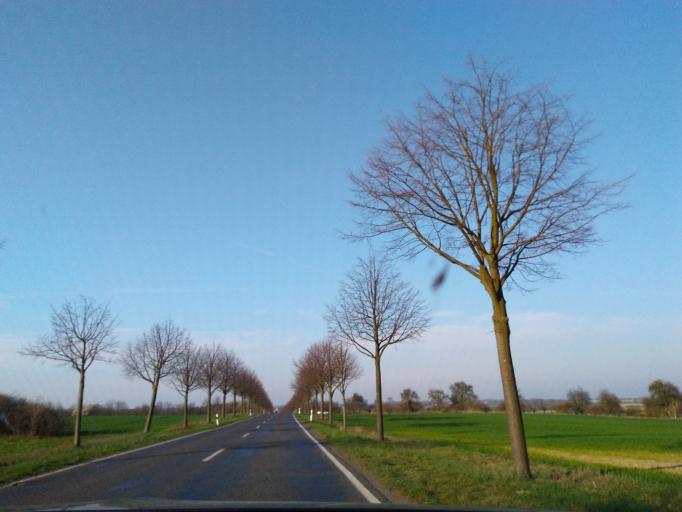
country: DE
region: Brandenburg
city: Waldsieversdorf
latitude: 52.5758
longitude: 14.0079
